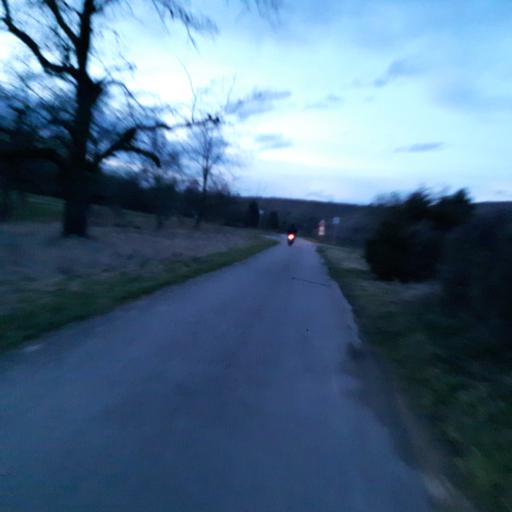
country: DE
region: Baden-Wuerttemberg
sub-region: Regierungsbezirk Stuttgart
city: Hessigheim
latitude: 48.9990
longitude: 9.1719
